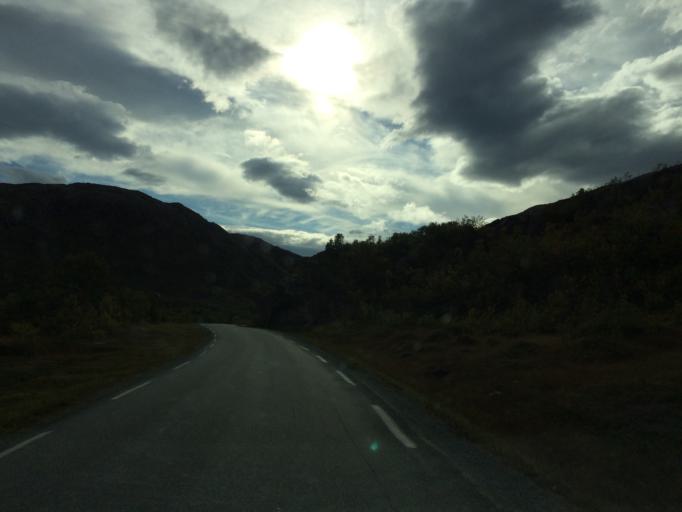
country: NO
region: Troms
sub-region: Lenvik
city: Finnsnes
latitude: 69.6134
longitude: 18.0761
